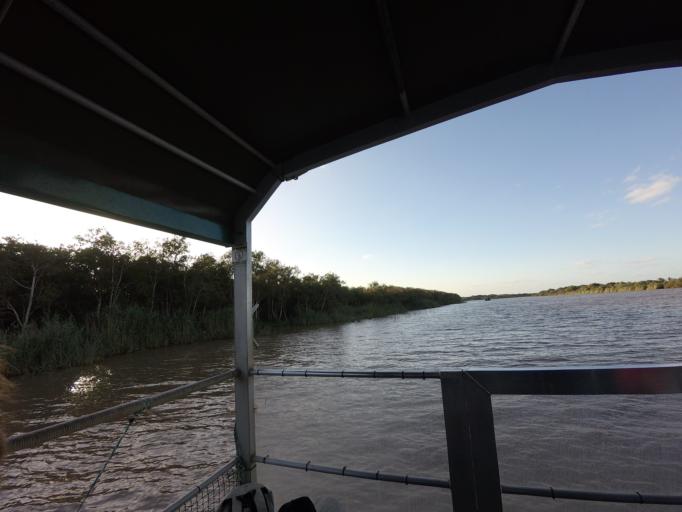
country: ZA
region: KwaZulu-Natal
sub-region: uMkhanyakude District Municipality
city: Mtubatuba
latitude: -28.3451
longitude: 32.4085
